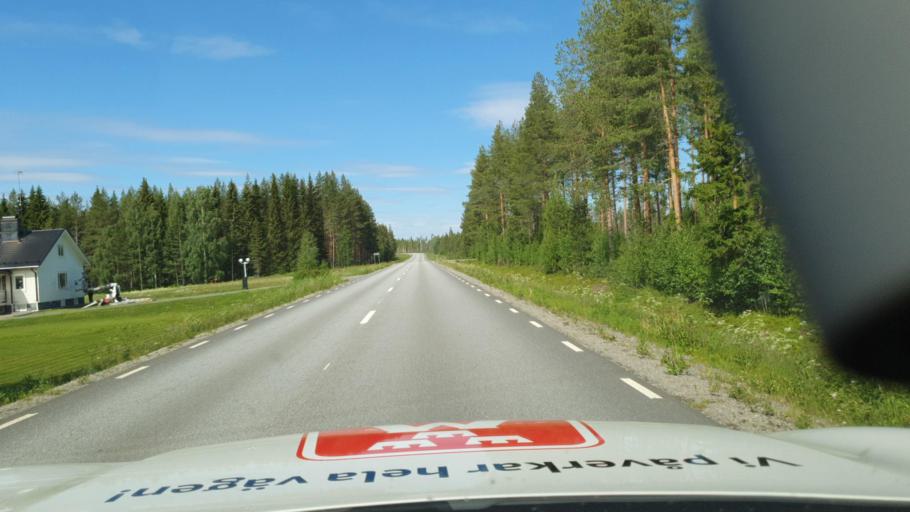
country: SE
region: Vaesterbotten
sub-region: Skelleftea Kommun
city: Forsbacka
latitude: 64.7298
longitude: 20.3970
